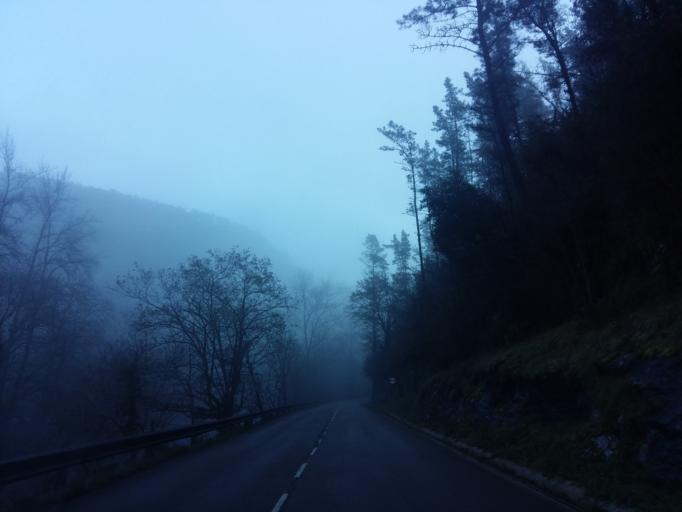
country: ES
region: Cantabria
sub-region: Provincia de Cantabria
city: Arredondo
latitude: 43.2762
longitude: -3.5811
